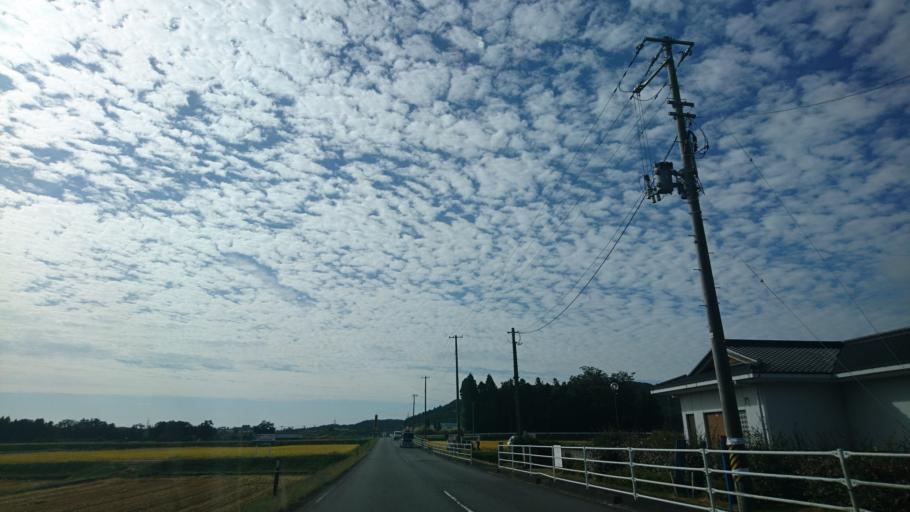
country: JP
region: Fukushima
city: Sukagawa
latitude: 37.3251
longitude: 140.2670
